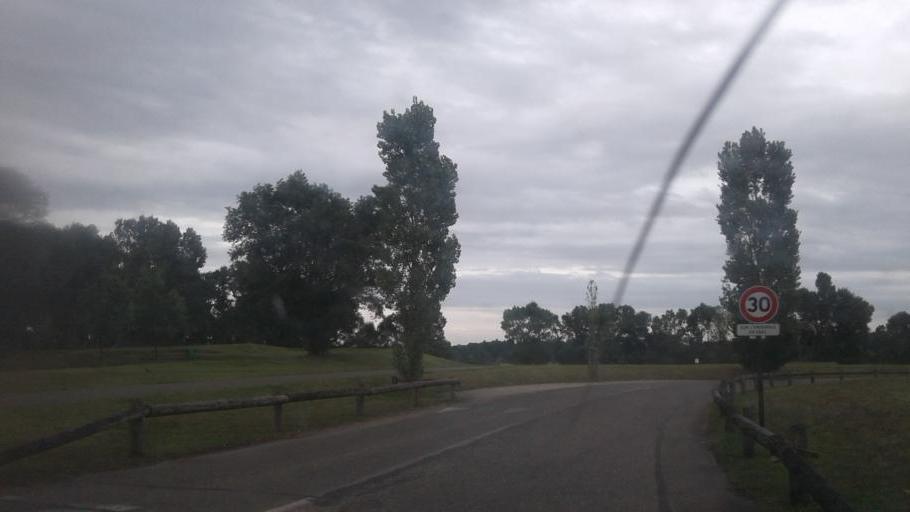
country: FR
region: Rhone-Alpes
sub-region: Departement du Rhone
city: Vaulx-en-Velin
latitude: 45.8063
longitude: 4.9331
